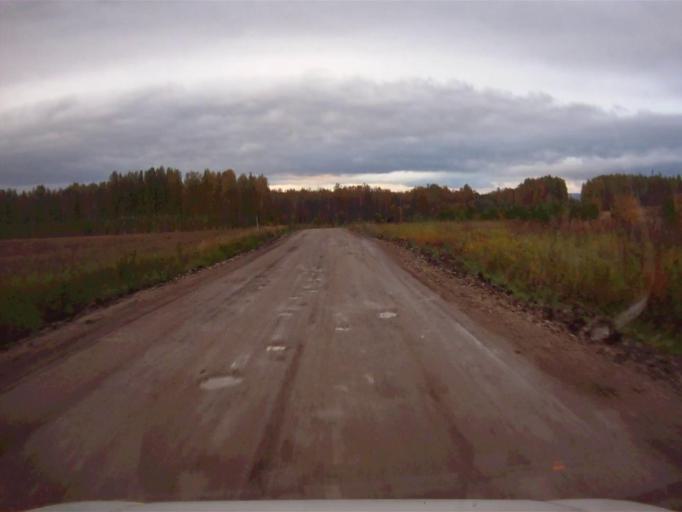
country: RU
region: Sverdlovsk
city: Mikhaylovsk
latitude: 56.1892
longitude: 59.1881
